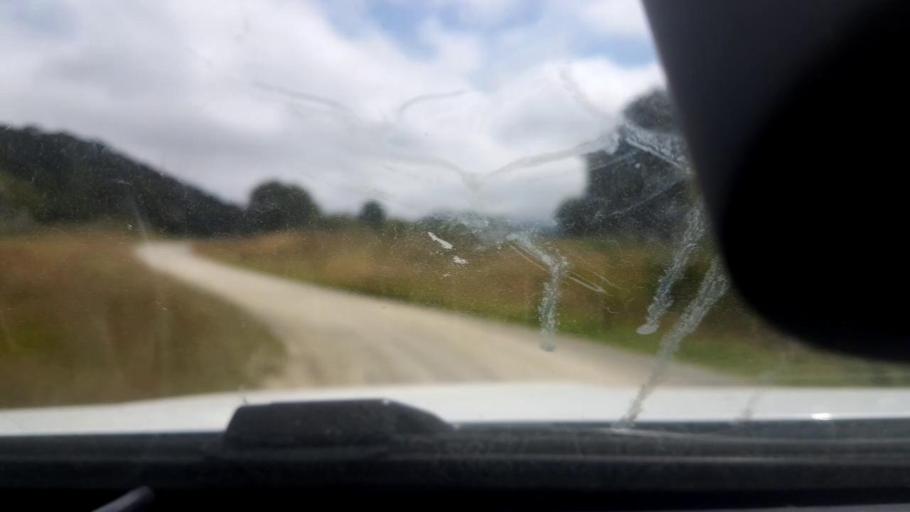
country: NZ
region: Canterbury
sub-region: Timaru District
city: Pleasant Point
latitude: -44.1530
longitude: 171.0916
